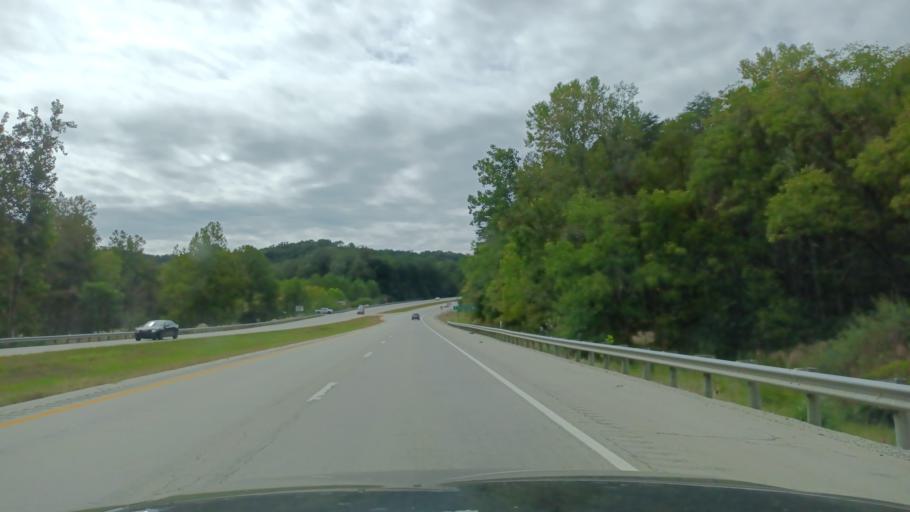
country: US
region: Ohio
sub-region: Washington County
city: Reno
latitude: 39.2513
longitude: -81.3030
